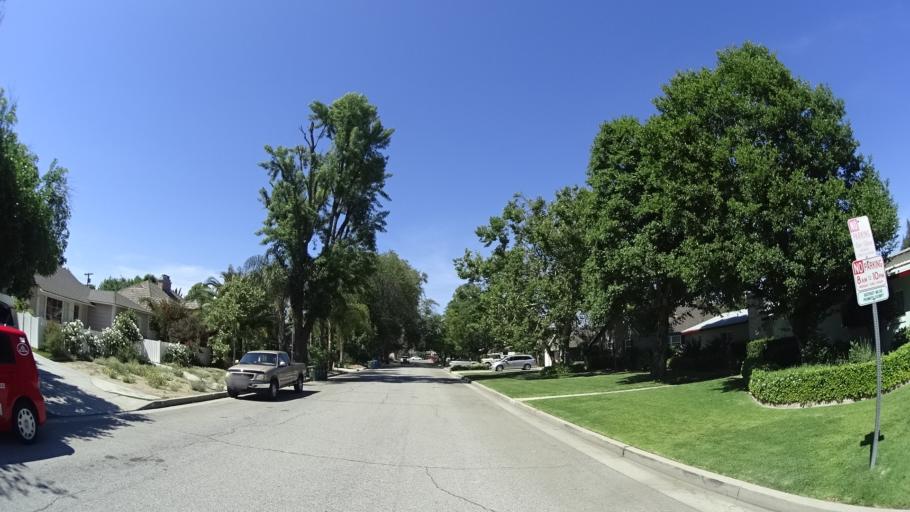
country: US
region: California
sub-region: Los Angeles County
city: Van Nuys
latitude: 34.1777
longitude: -118.4237
